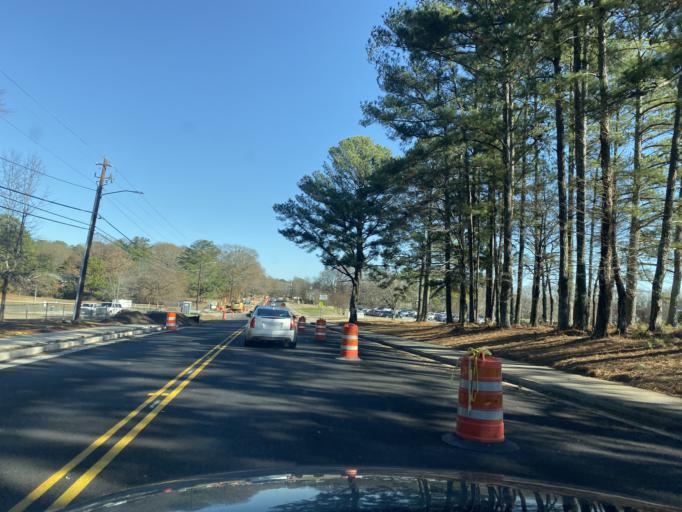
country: US
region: Georgia
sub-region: DeKalb County
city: Pine Mountain
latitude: 33.6785
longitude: -84.1729
